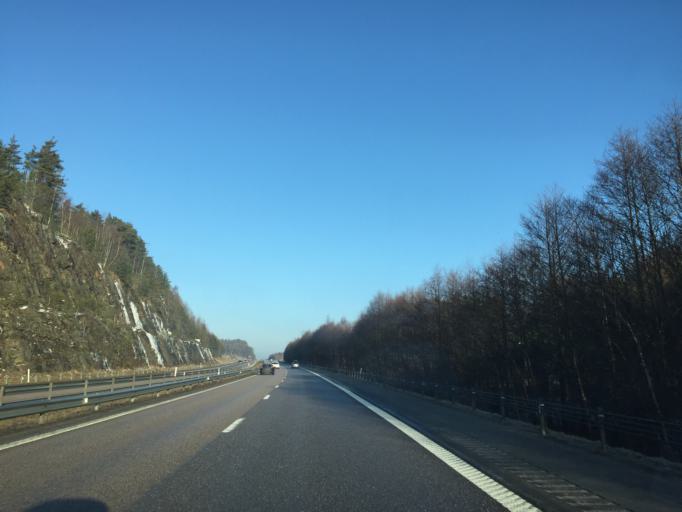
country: SE
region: Vaestra Goetaland
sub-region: Uddevalla Kommun
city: Ljungskile
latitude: 58.2438
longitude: 11.9092
